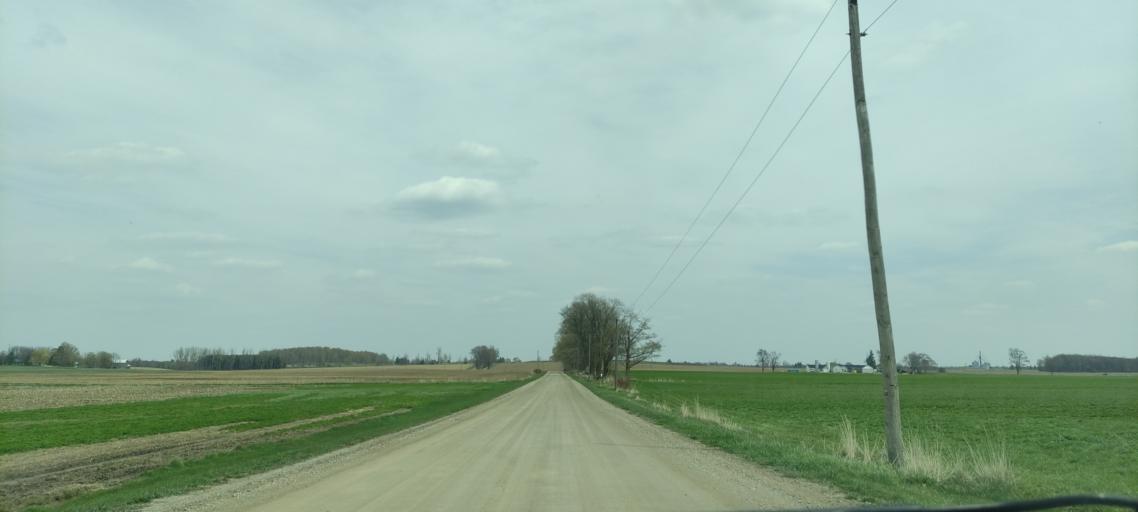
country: CA
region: Ontario
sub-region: Oxford County
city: Woodstock
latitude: 43.2818
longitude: -80.6716
